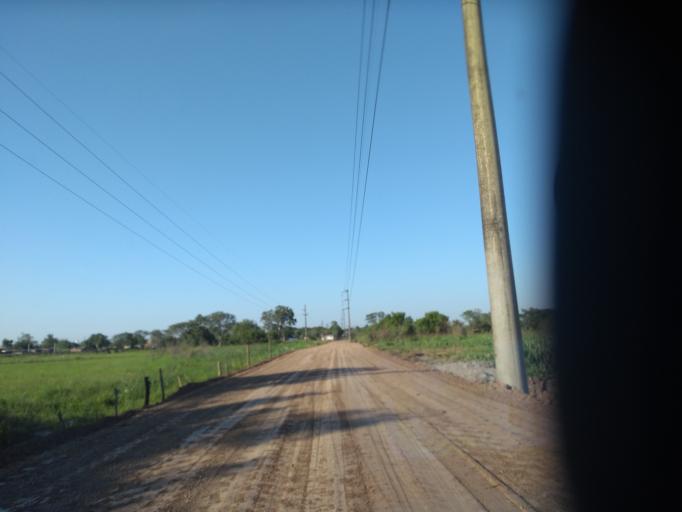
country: AR
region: Chaco
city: Fontana
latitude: -27.4134
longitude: -59.0181
